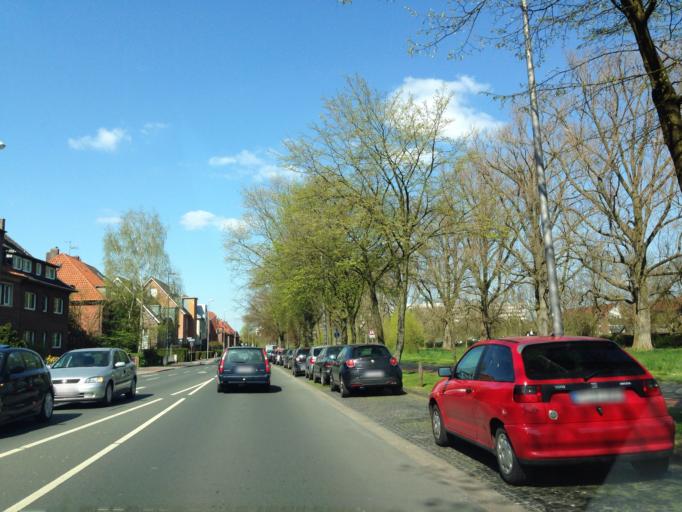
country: DE
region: North Rhine-Westphalia
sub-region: Regierungsbezirk Munster
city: Muenster
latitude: 51.9734
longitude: 7.6330
